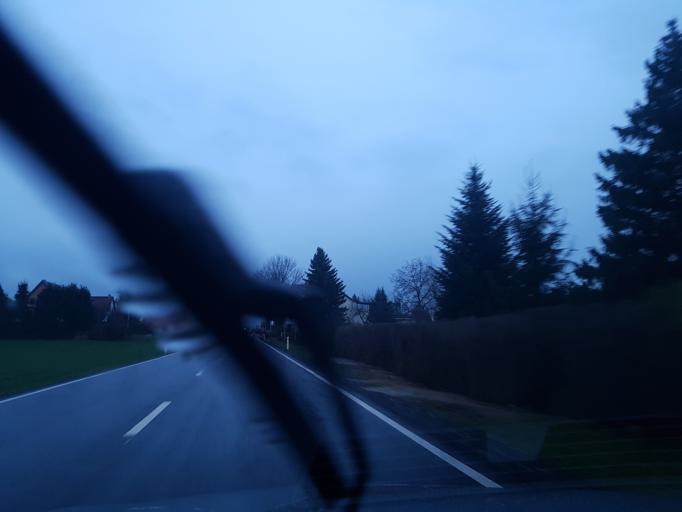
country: DE
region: Saxony
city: Priestewitz
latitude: 51.2570
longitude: 13.5105
